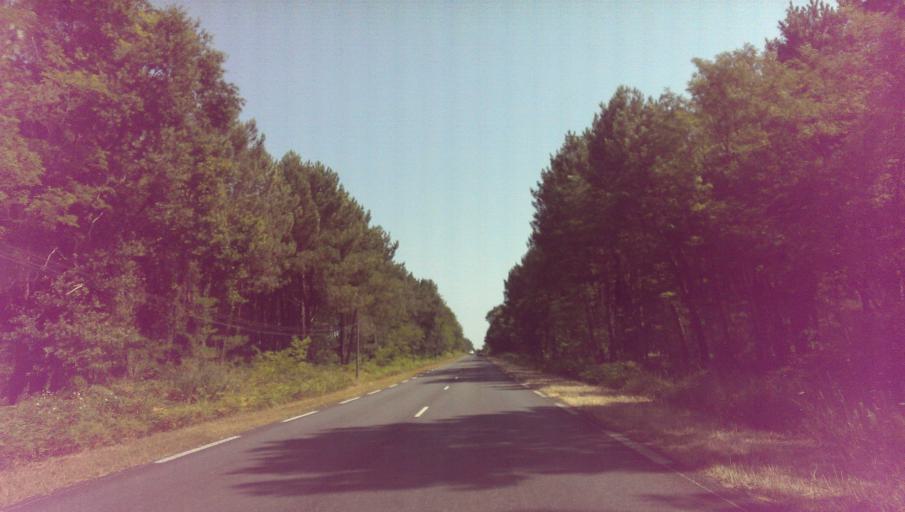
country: FR
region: Aquitaine
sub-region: Departement des Landes
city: Sarbazan
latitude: 44.0017
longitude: -0.2051
